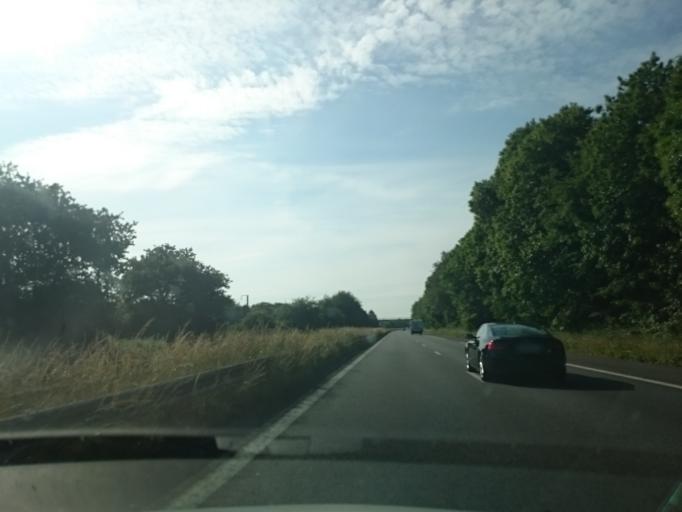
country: FR
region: Brittany
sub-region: Departement du Finistere
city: Redene
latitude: 47.8274
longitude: -3.4757
